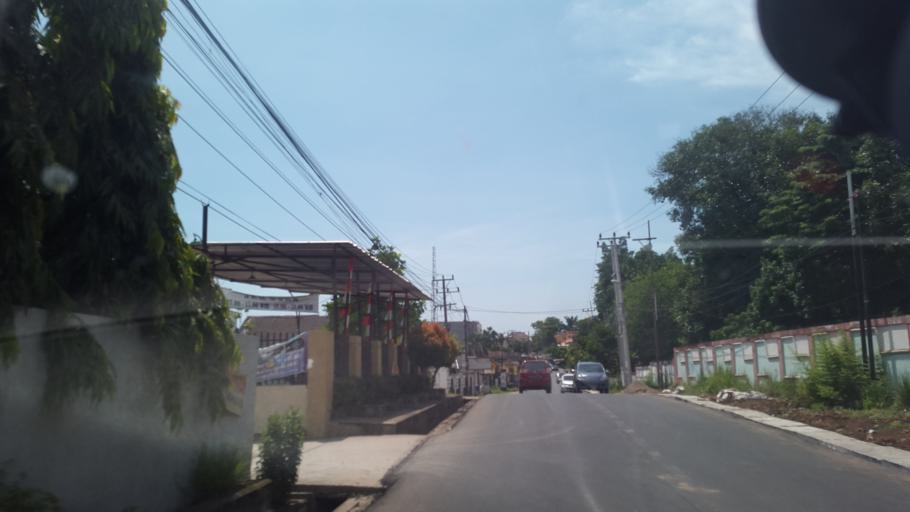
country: ID
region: South Sumatra
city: Plaju
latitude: -2.9976
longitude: 104.7273
